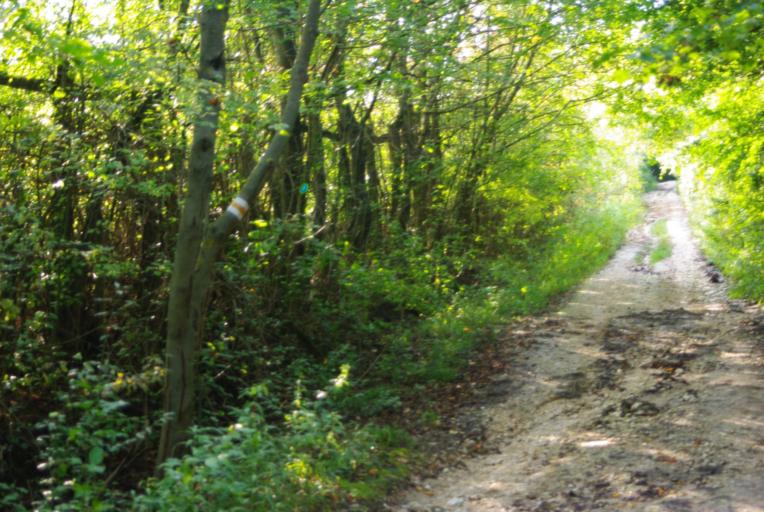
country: HU
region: Pest
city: Pilisszentivan
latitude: 47.5808
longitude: 18.8640
